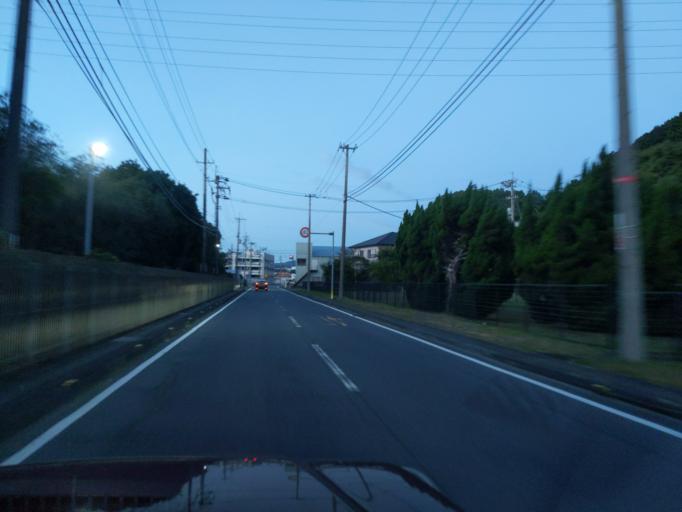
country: JP
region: Tokushima
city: Anan
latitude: 33.8797
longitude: 134.6515
